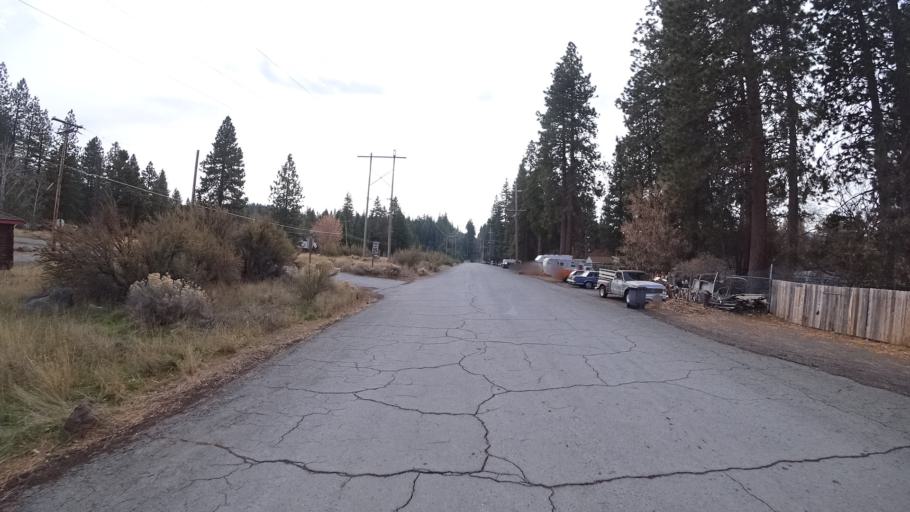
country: US
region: California
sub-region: Siskiyou County
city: Weed
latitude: 41.4479
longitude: -122.3622
